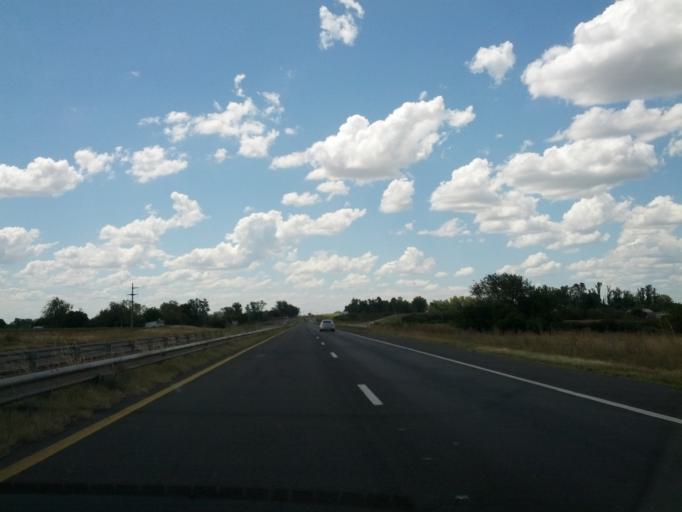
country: AR
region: Entre Rios
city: Concepcion del Uruguay
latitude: -32.3972
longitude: -58.2785
